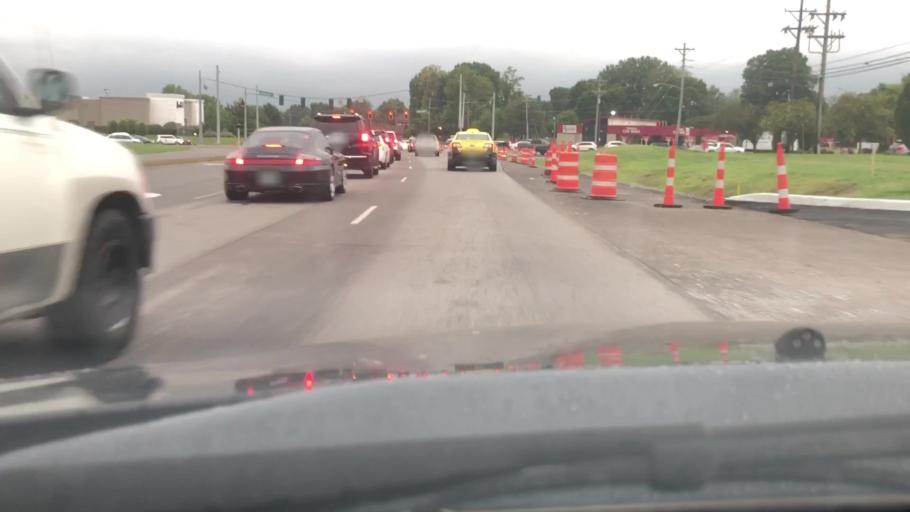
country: US
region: Kentucky
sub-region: Jefferson County
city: Hurstbourne Acres
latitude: 38.2149
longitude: -85.5898
